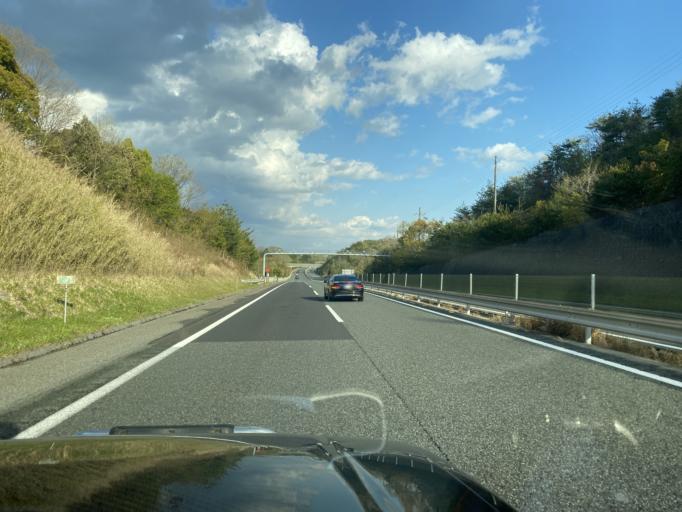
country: JP
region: Hyogo
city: Sandacho
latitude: 34.9445
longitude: 135.1478
